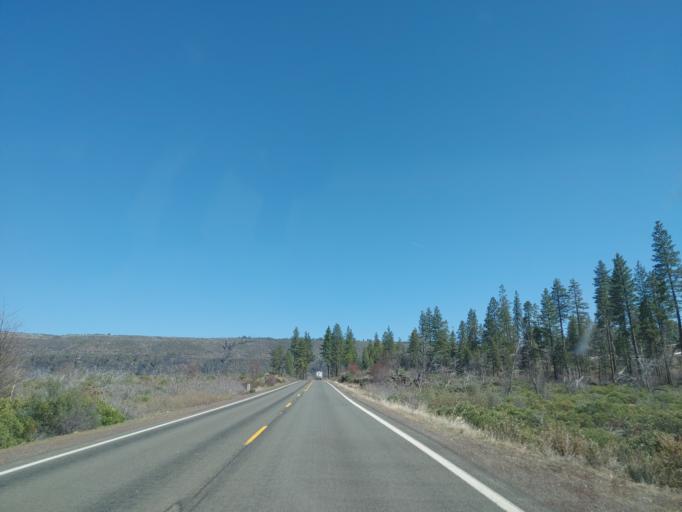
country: US
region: California
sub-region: Shasta County
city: Burney
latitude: 40.7304
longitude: -121.4356
